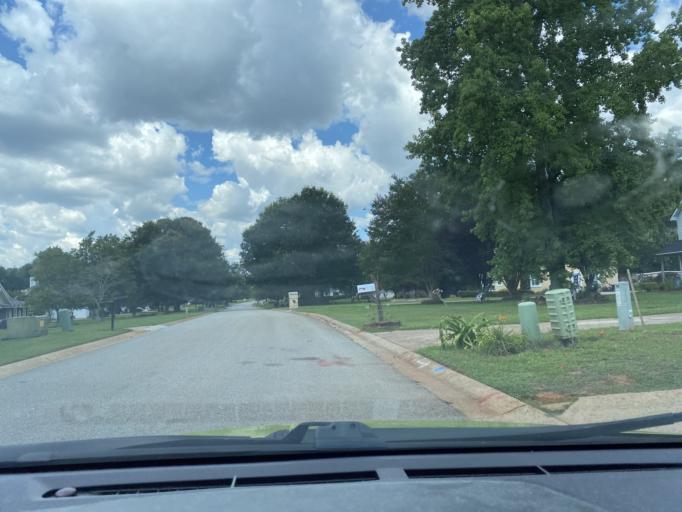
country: US
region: Georgia
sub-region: Fayette County
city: Peachtree City
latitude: 33.4115
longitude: -84.6760
